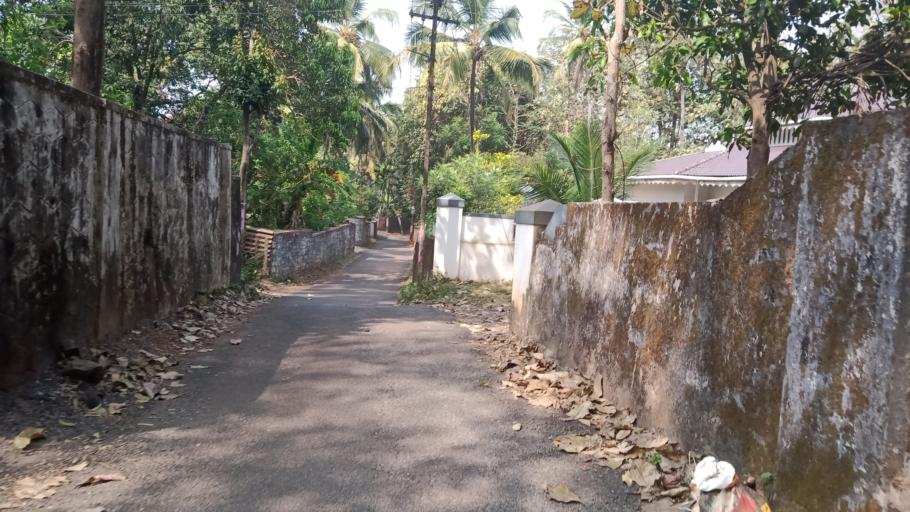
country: IN
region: Kerala
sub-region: Palakkad district
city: Cherpulassery
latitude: 10.8823
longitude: 76.3136
